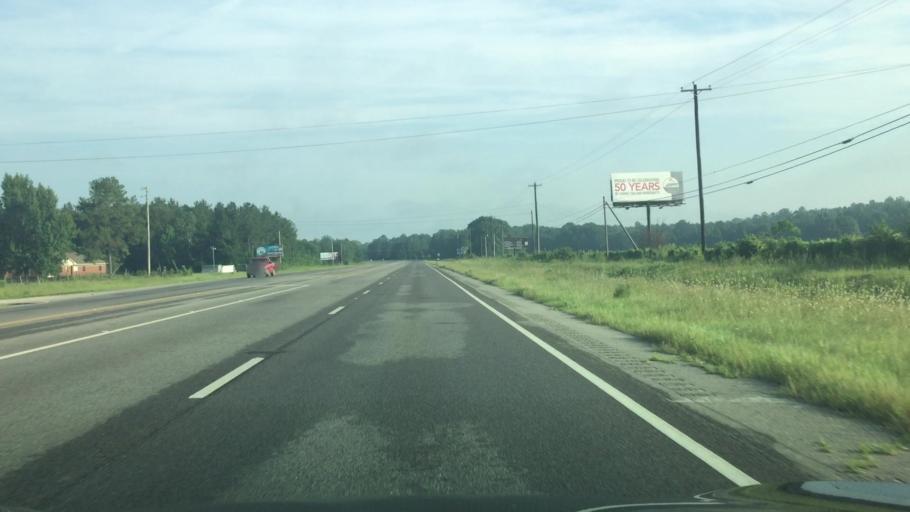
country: US
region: Alabama
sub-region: Covington County
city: Andalusia
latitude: 31.3403
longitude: -86.5227
